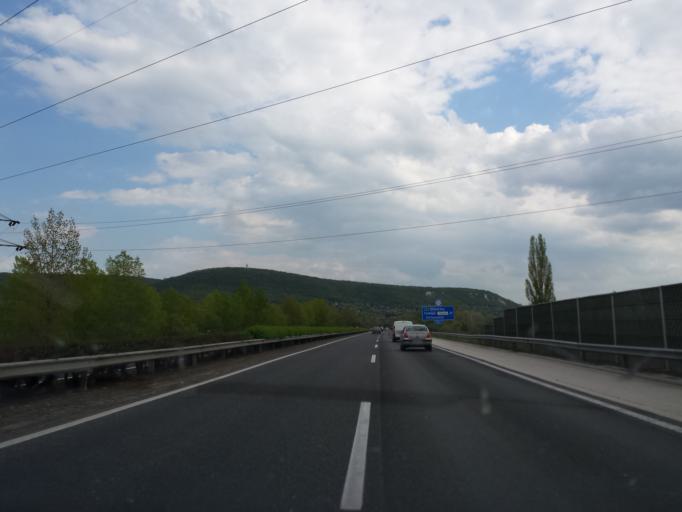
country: HU
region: Komarom-Esztergom
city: Vertesszolos
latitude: 47.6033
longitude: 18.3788
